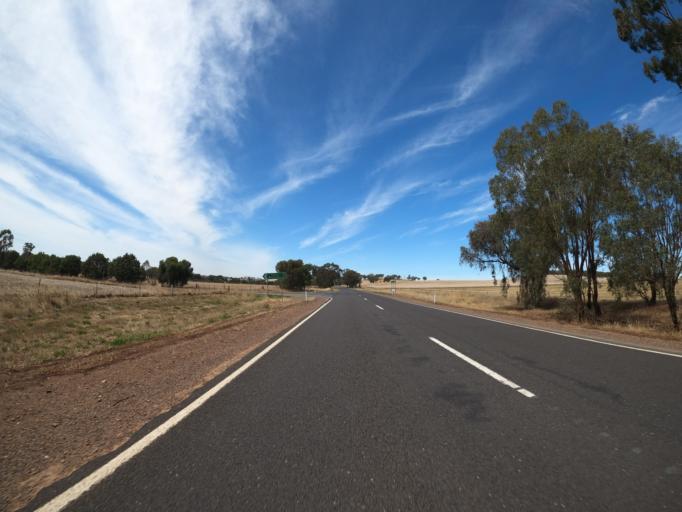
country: AU
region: Victoria
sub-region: Benalla
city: Benalla
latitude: -36.3169
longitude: 145.9583
